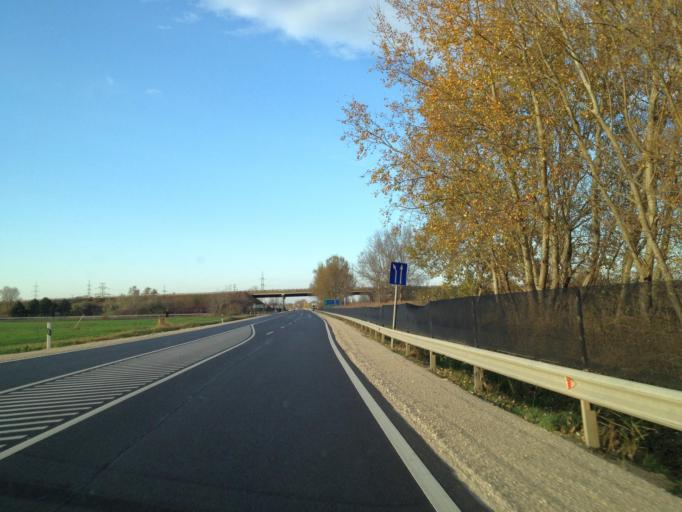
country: HU
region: Gyor-Moson-Sopron
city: Gyorujbarat
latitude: 47.6299
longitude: 17.6720
